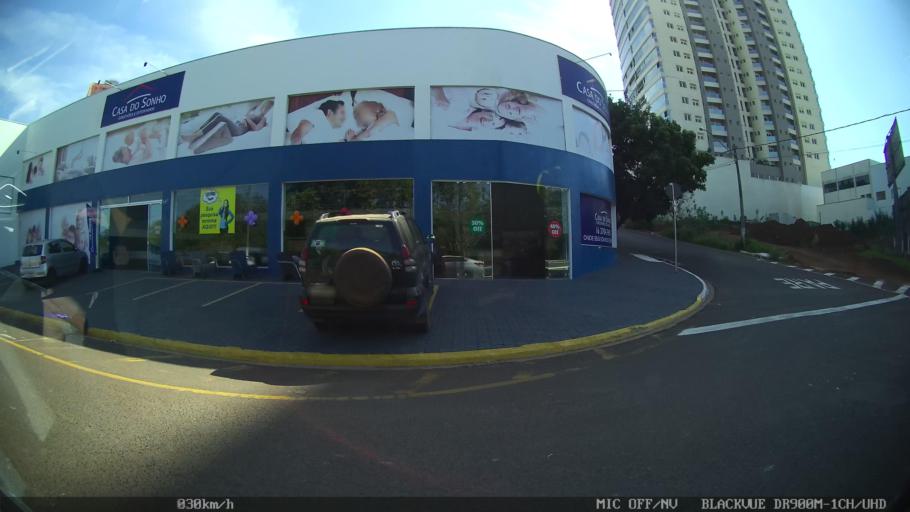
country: BR
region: Sao Paulo
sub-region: Franca
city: Franca
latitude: -20.5543
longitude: -47.4139
